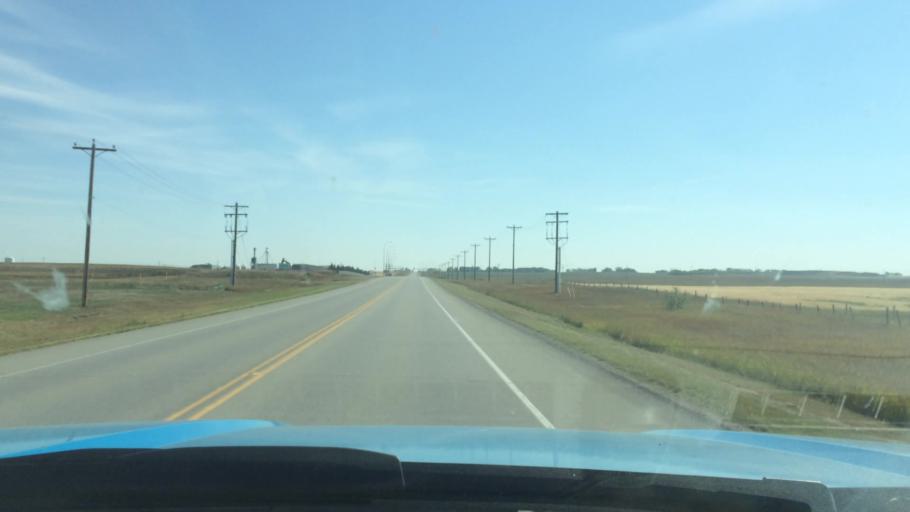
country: CA
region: Alberta
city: Airdrie
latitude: 51.2126
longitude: -113.9440
